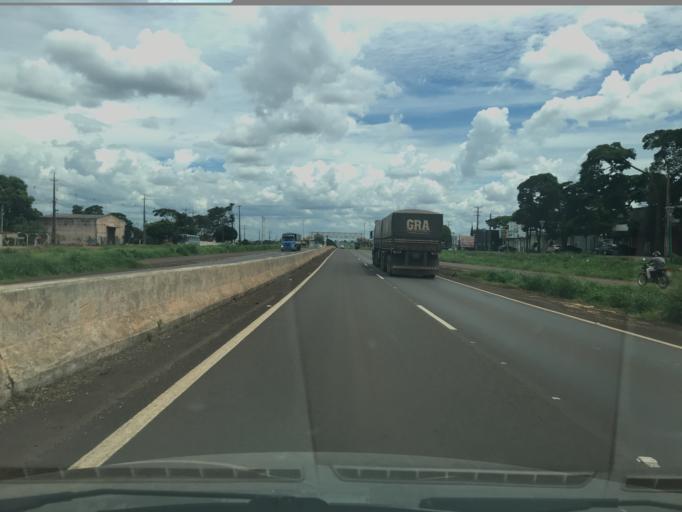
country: BR
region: Parana
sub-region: Paicandu
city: Paicandu
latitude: -23.4603
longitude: -52.0334
